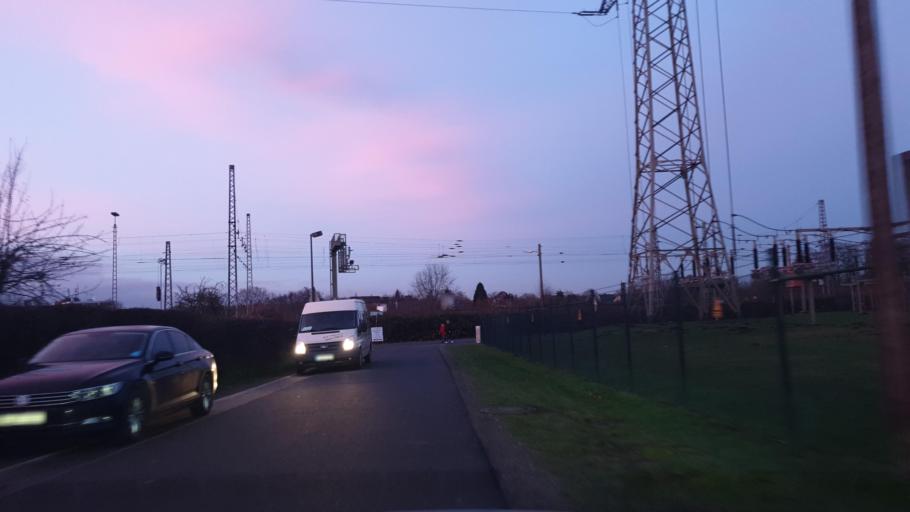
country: DE
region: Lower Saxony
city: Osnabrueck
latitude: 52.2603
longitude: 8.0345
